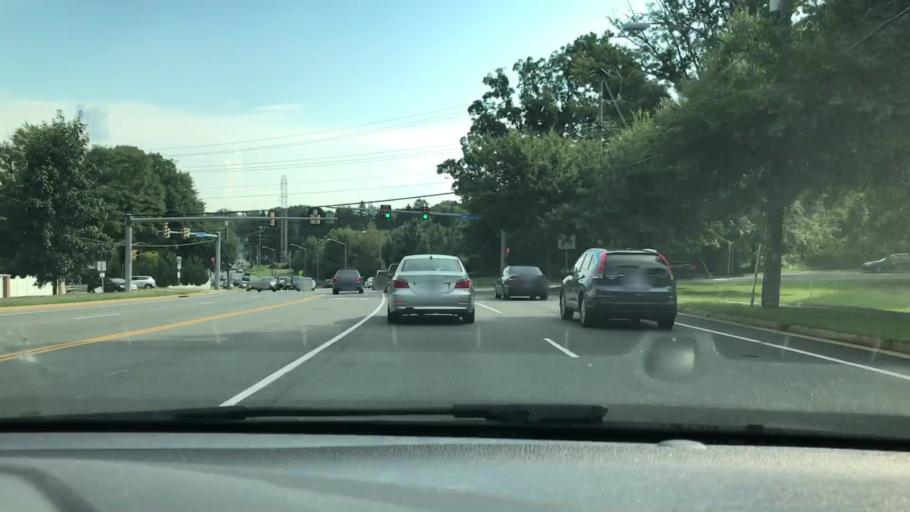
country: US
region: Virginia
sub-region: Fairfax County
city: Dunn Loring
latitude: 38.8956
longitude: -77.2252
